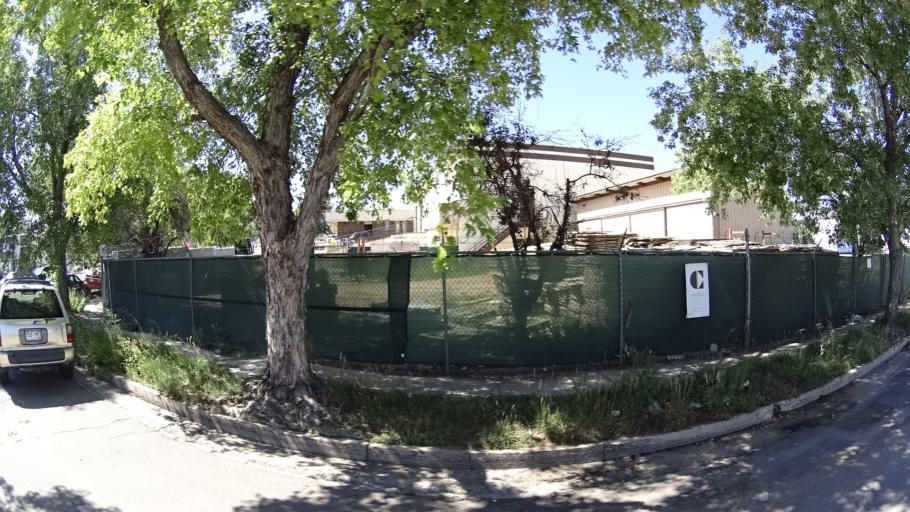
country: US
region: Colorado
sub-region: El Paso County
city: Colorado Springs
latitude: 38.8373
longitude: -104.7645
